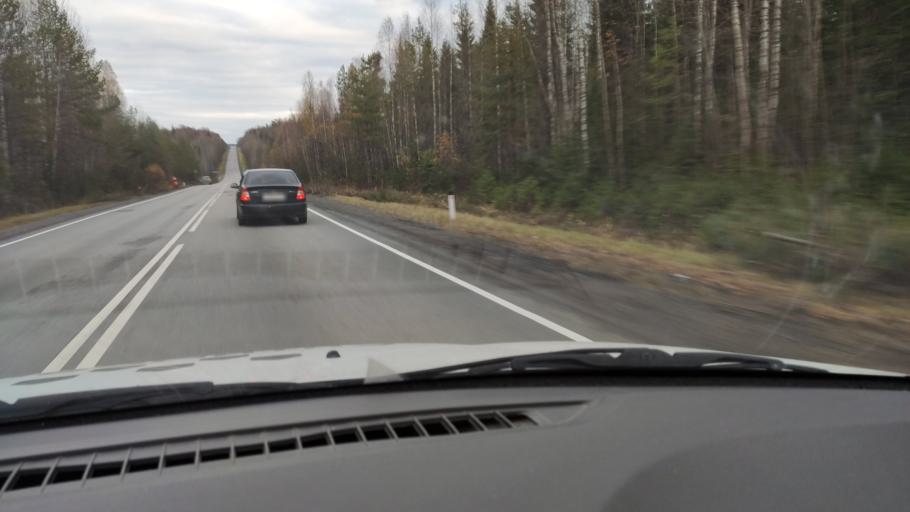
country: RU
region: Kirov
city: Chernaya Kholunitsa
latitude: 58.8653
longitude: 51.5781
